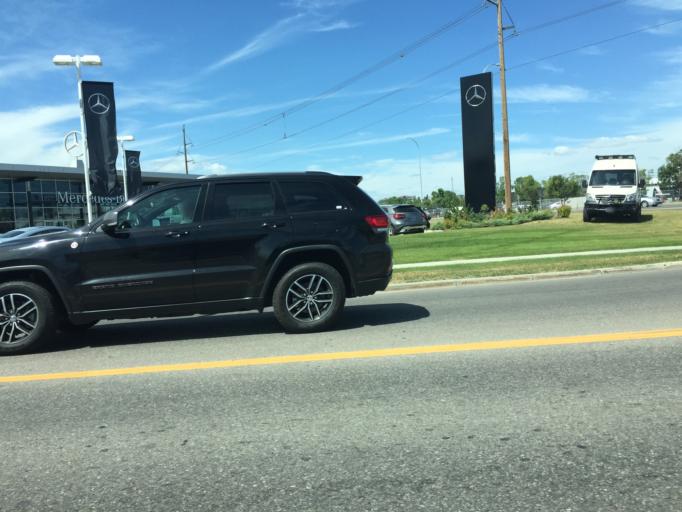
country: CA
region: Alberta
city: Calgary
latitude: 50.9865
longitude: -114.0294
